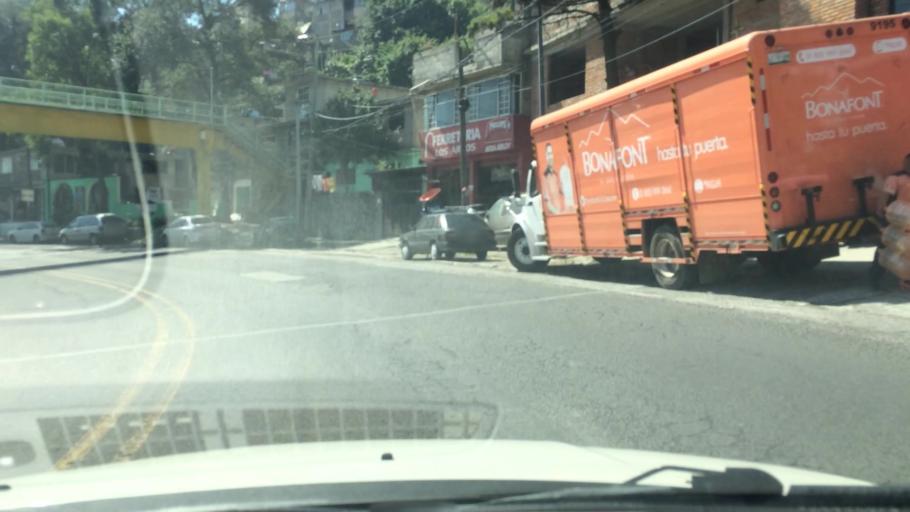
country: MX
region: Mexico City
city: Tlalpan
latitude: 19.2505
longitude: -99.1764
